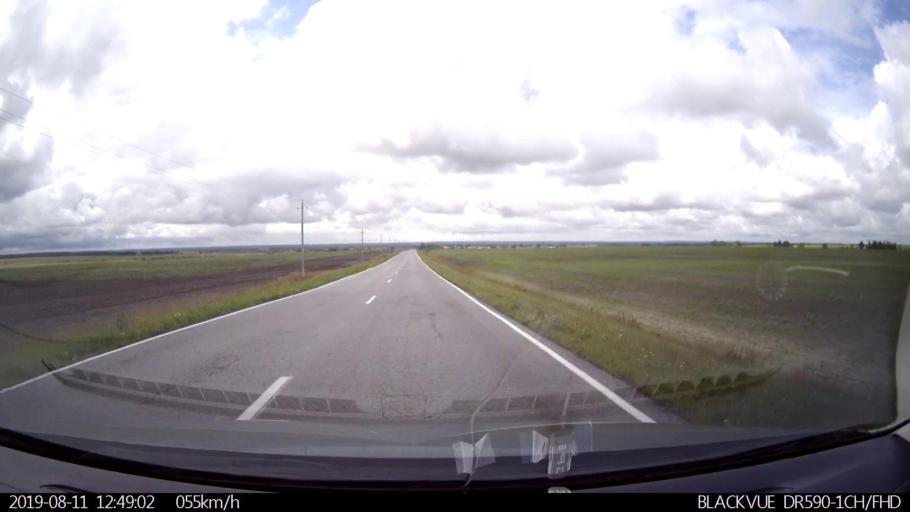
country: RU
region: Ulyanovsk
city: Ignatovka
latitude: 53.8748
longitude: 47.6934
